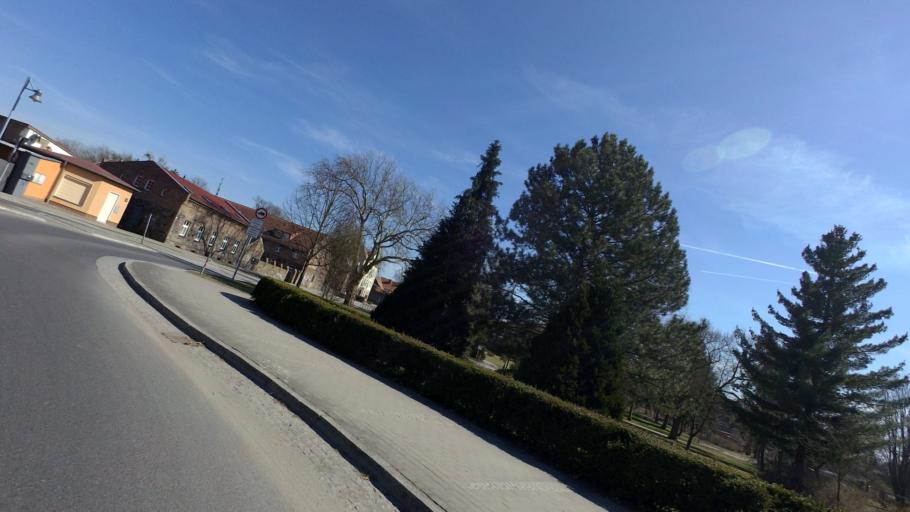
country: DE
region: Brandenburg
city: Muncheberg
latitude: 52.5055
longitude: 14.1361
